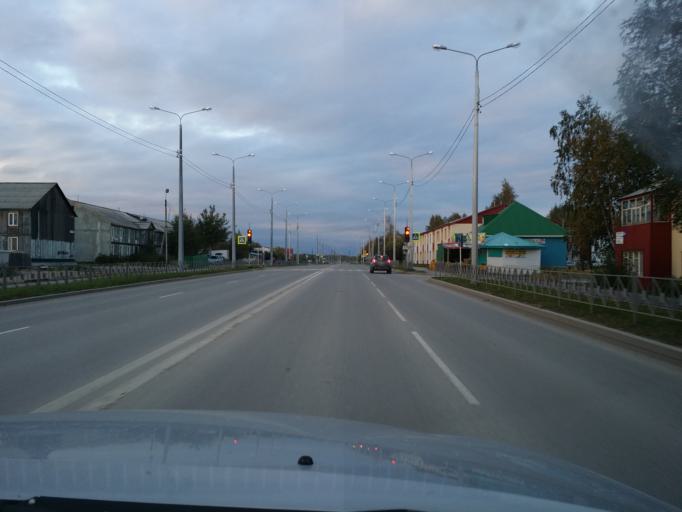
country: RU
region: Khanty-Mansiyskiy Avtonomnyy Okrug
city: Megion
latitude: 61.0362
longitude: 76.0958
